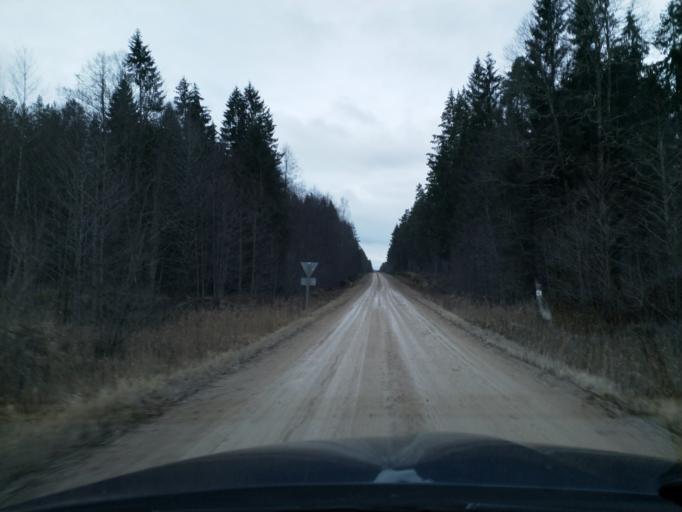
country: LV
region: Kuldigas Rajons
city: Kuldiga
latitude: 56.9517
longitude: 22.2480
